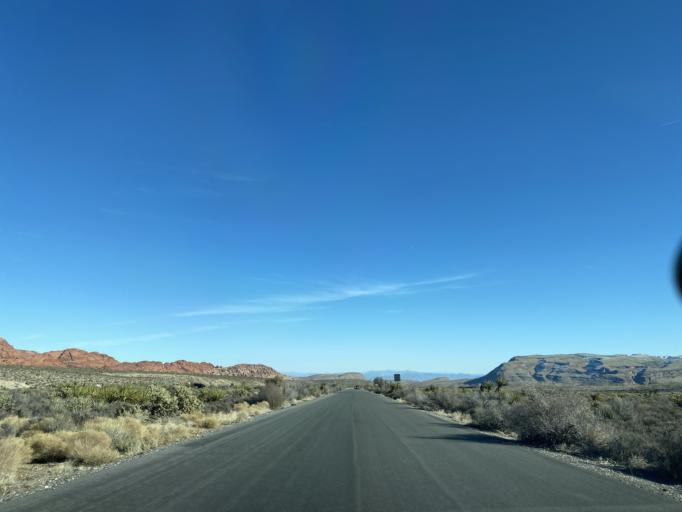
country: US
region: Nevada
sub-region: Clark County
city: Summerlin South
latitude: 36.1406
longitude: -115.4719
